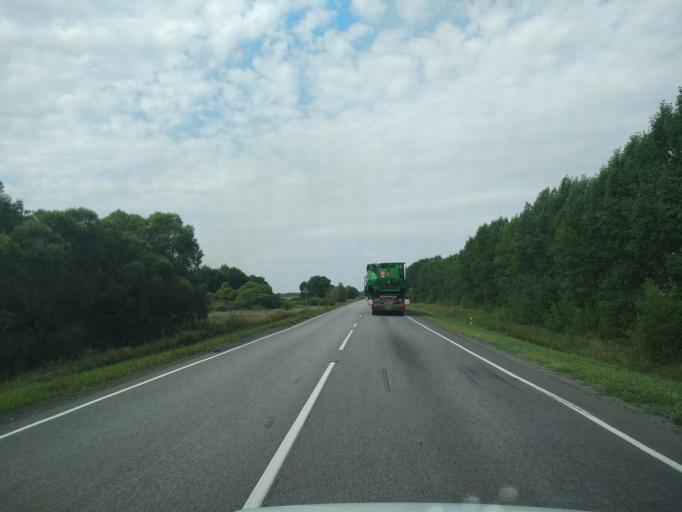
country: RU
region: Voronezj
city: Pereleshinskiy
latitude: 51.8752
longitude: 40.4061
